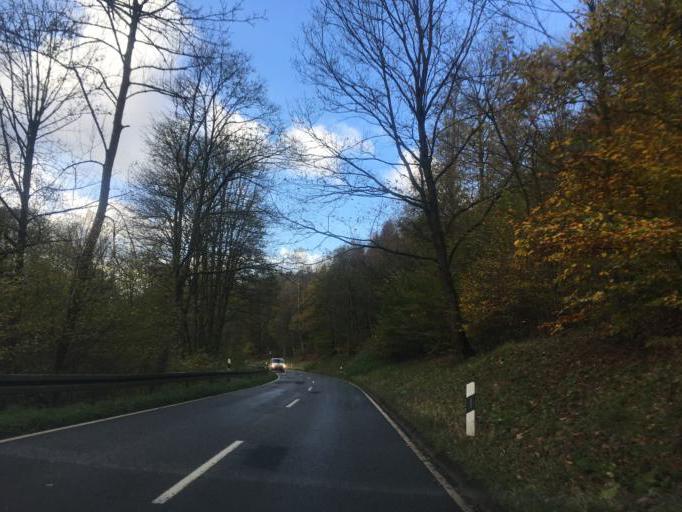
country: DE
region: Lower Saxony
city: Furstenberg
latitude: 51.7547
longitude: 9.4446
